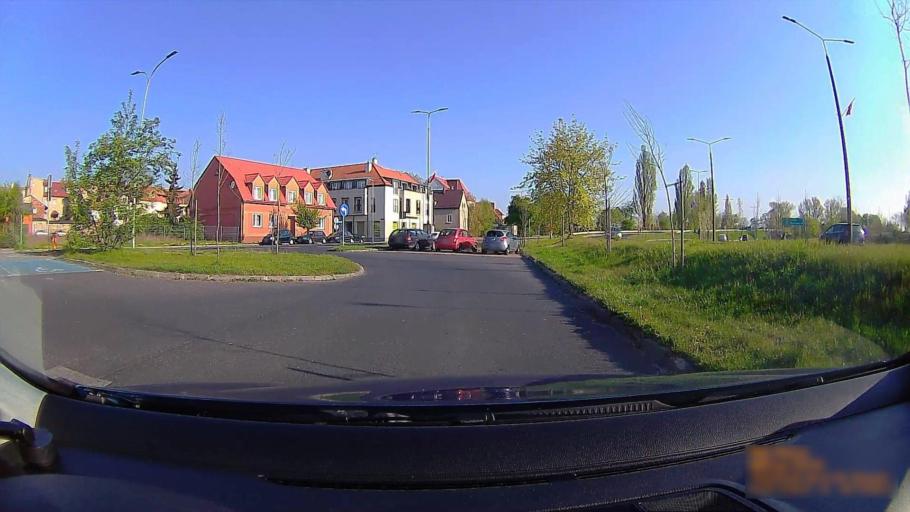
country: PL
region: Greater Poland Voivodeship
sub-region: Konin
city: Konin
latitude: 52.2098
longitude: 18.2572
